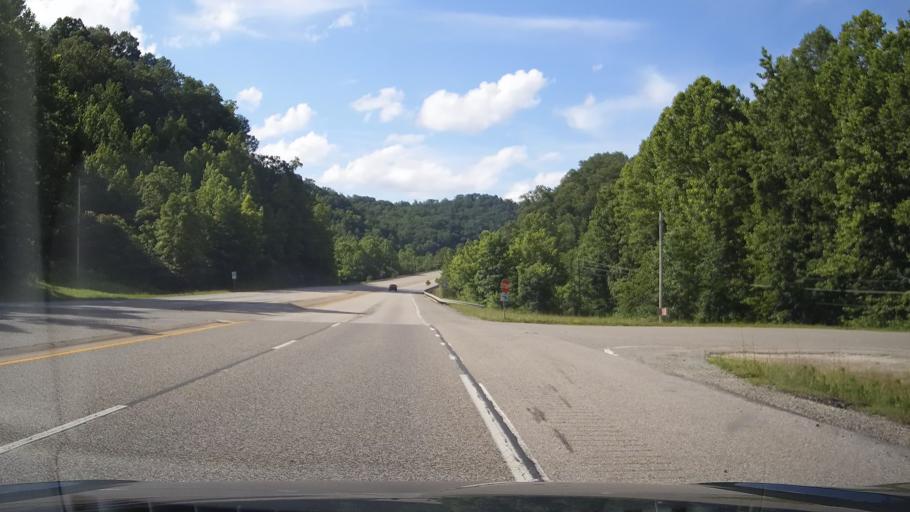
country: US
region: Kentucky
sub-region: Lawrence County
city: Louisa
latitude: 38.0237
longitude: -82.6515
